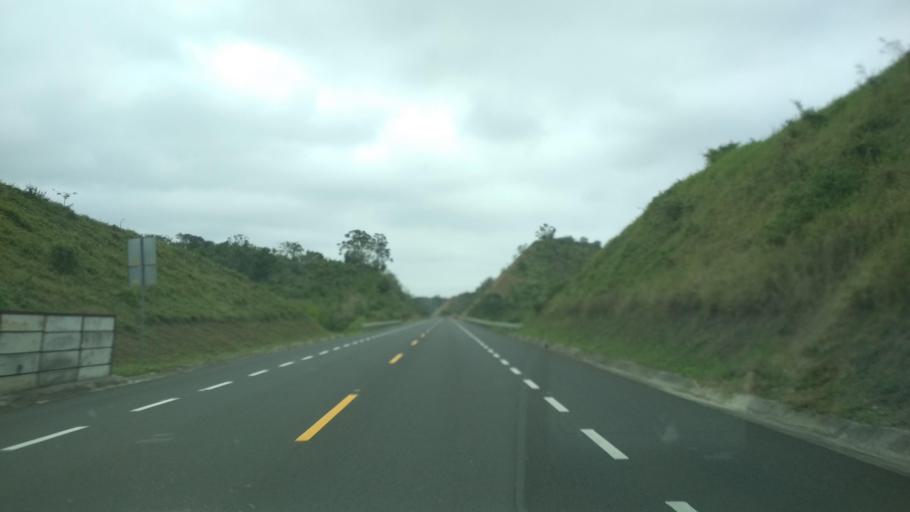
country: MX
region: Veracruz
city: Gutierrez Zamora
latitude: 20.2934
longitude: -97.0749
